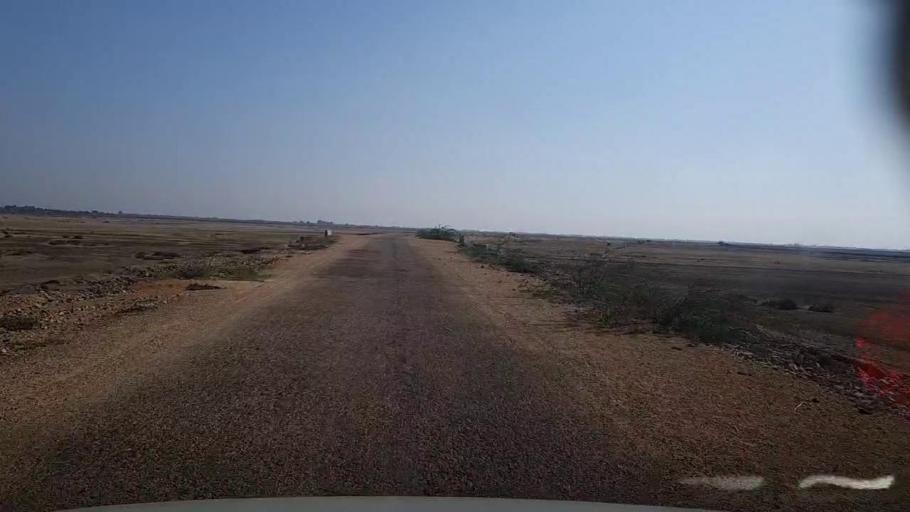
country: PK
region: Sindh
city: Mirpur Sakro
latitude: 24.5172
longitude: 67.4985
